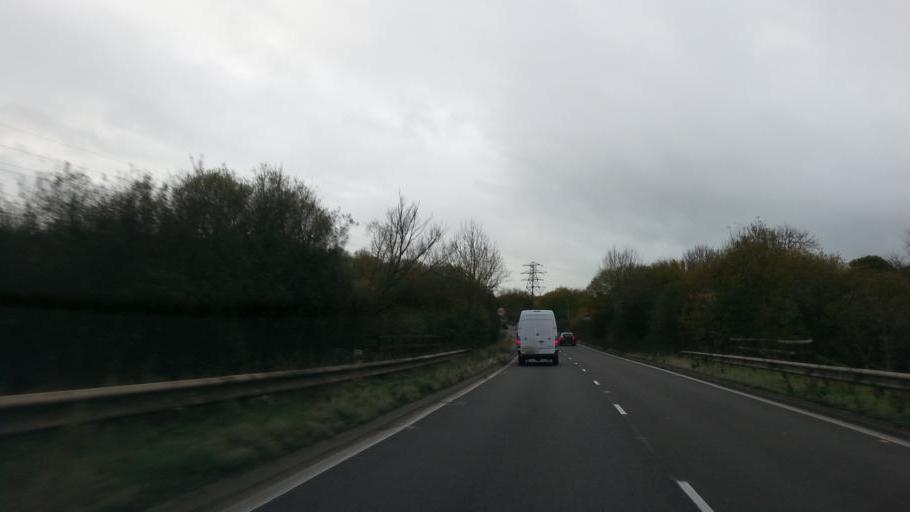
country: GB
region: England
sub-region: Northamptonshire
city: Kettering
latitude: 52.4391
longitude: -0.7351
